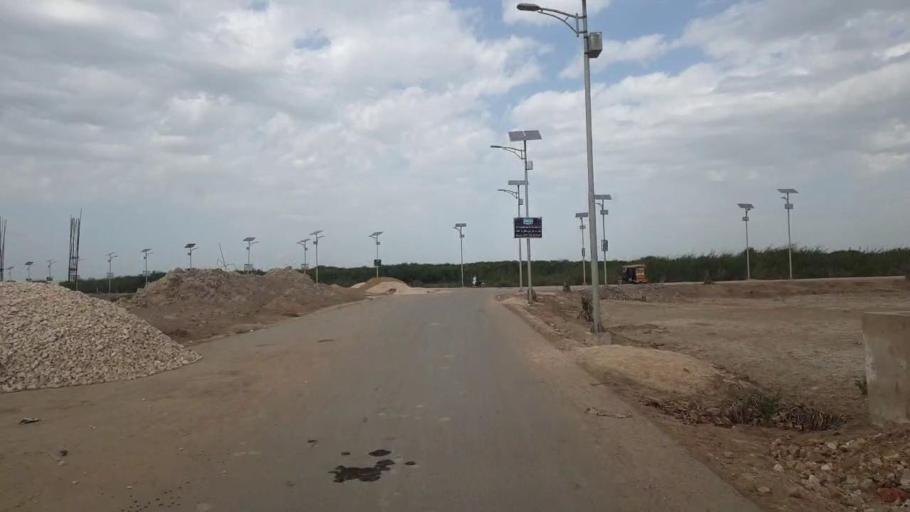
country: PK
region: Sindh
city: Hala
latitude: 25.9345
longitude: 68.4036
